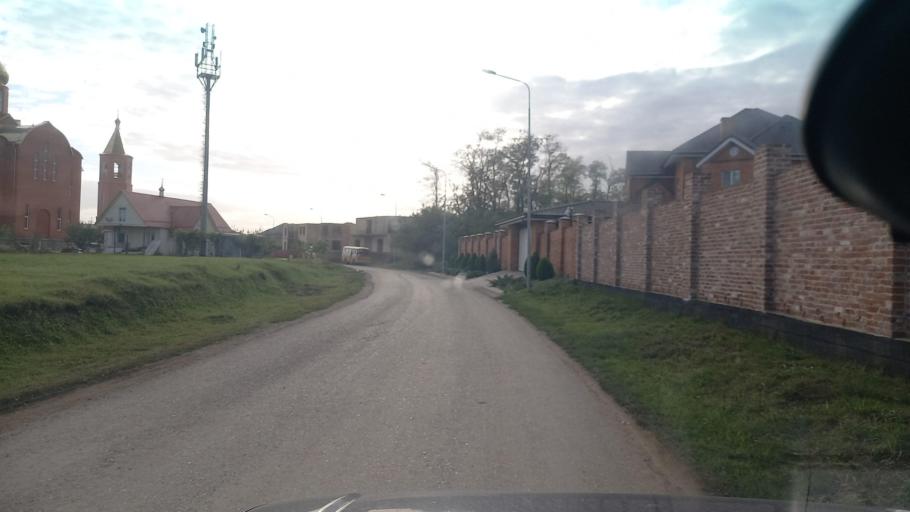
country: RU
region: Krasnodarskiy
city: Krasnodar
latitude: 45.1226
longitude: 38.9246
